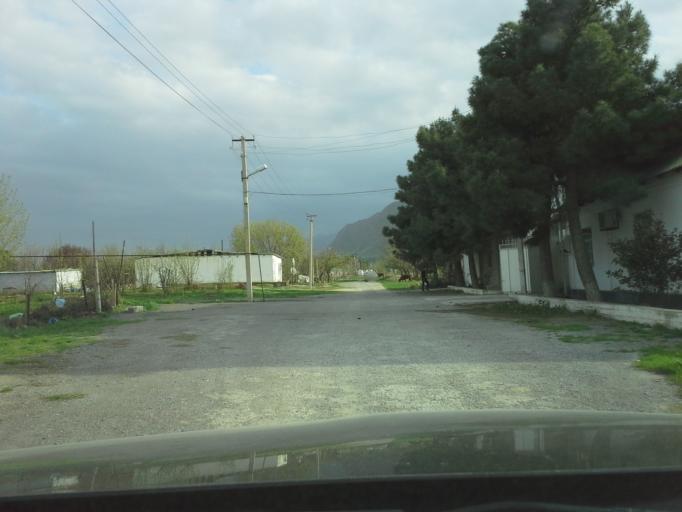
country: TM
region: Ahal
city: Abadan
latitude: 37.9329
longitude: 58.2261
